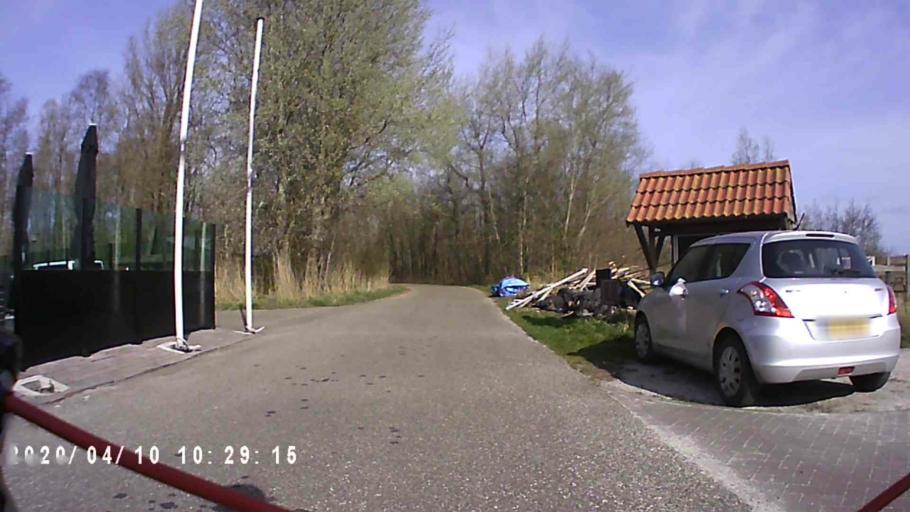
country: NL
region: Friesland
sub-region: Gemeente Dongeradeel
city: Anjum
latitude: 53.3902
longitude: 6.2151
